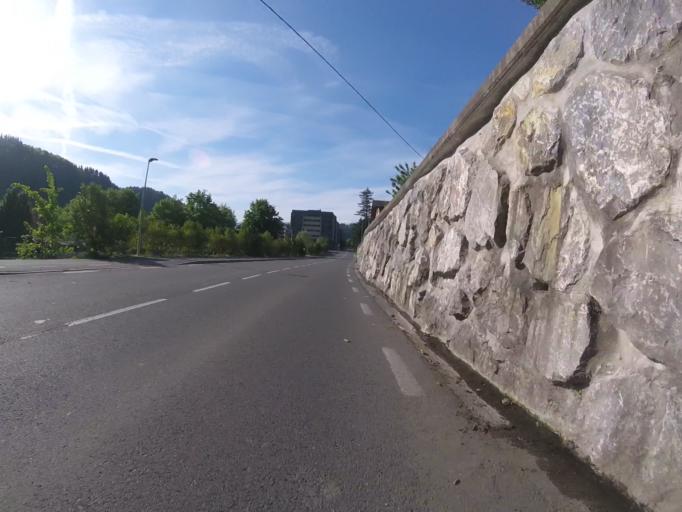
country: ES
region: Basque Country
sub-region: Provincia de Guipuzcoa
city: Arama
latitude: 43.0625
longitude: -2.1734
